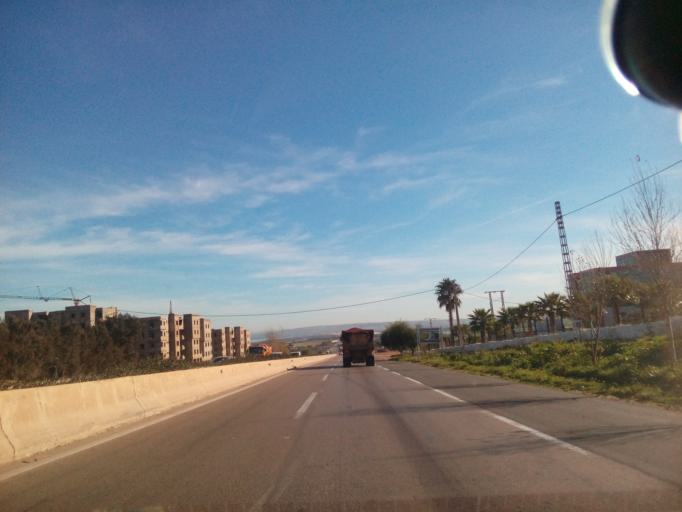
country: DZ
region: Oran
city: Ain el Bya
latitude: 35.7864
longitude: -0.1744
